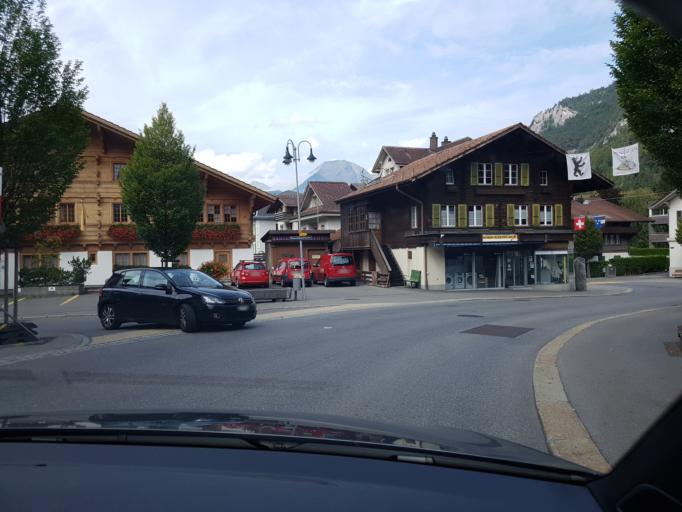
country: CH
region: Bern
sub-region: Interlaken-Oberhasli District
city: Meiringen
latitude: 46.7256
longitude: 8.1902
